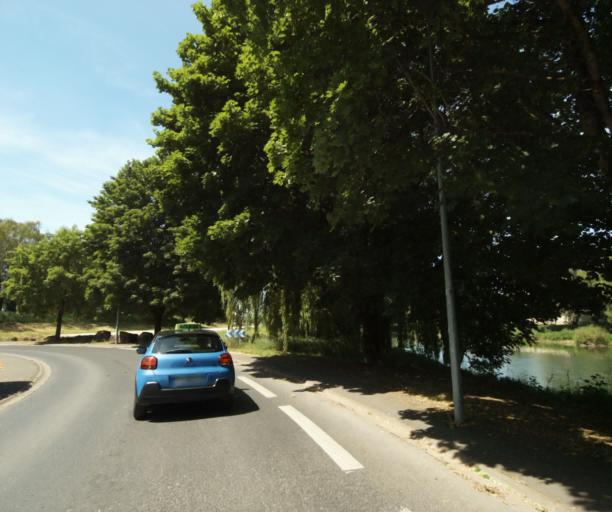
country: FR
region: Champagne-Ardenne
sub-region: Departement des Ardennes
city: Charleville-Mezieres
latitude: 49.7588
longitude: 4.7117
